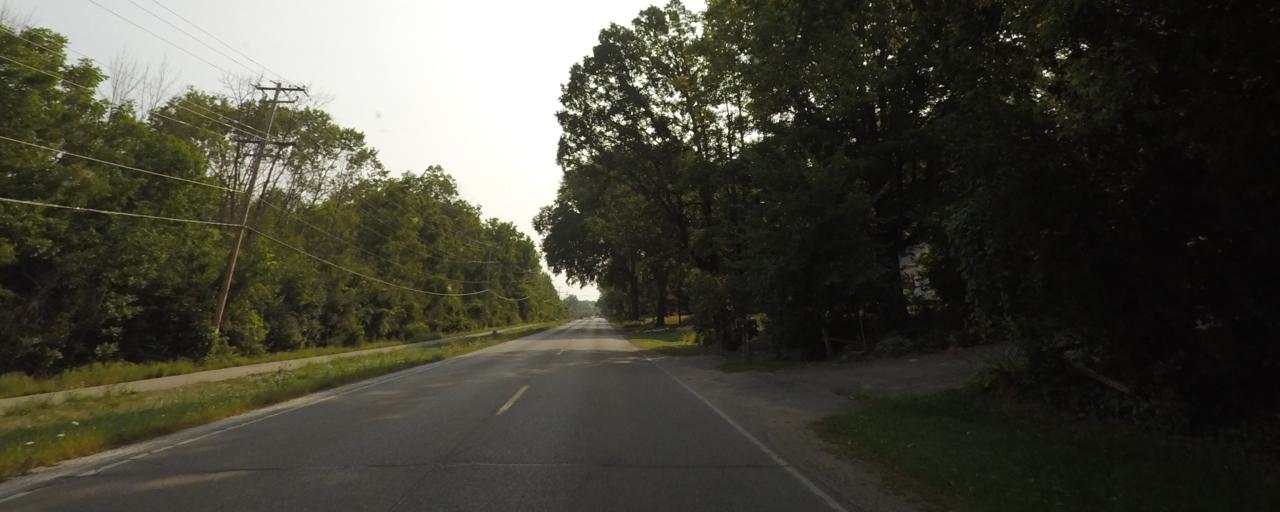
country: US
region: Wisconsin
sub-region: Waukesha County
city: Delafield
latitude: 43.0591
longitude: -88.4185
